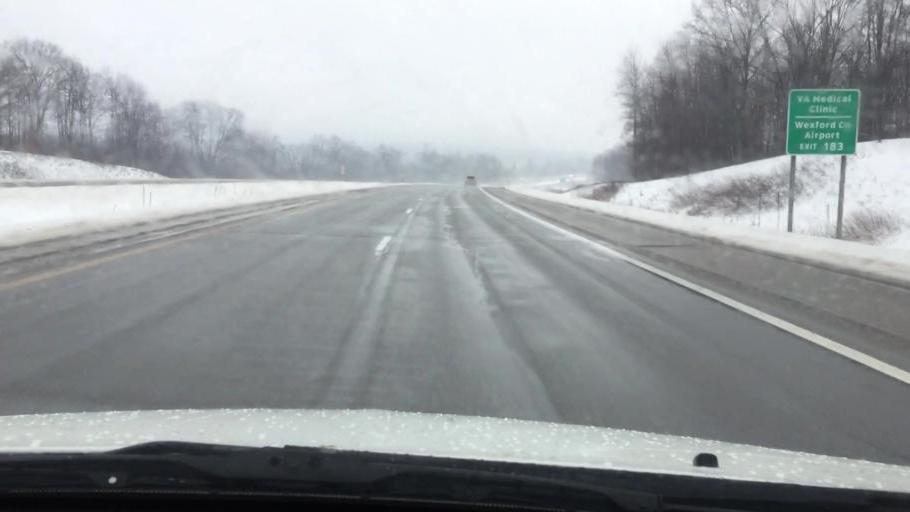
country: US
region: Michigan
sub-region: Wexford County
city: Cadillac
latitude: 44.2953
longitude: -85.3900
